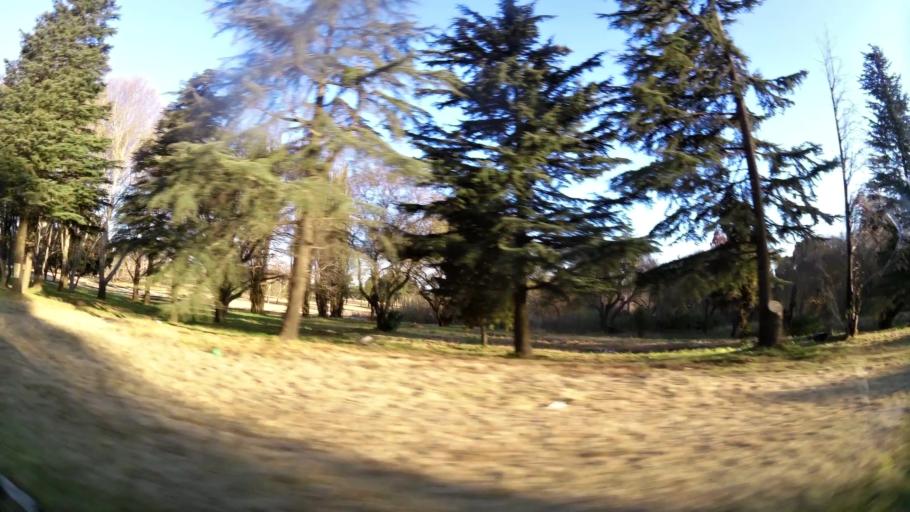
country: ZA
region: Gauteng
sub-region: City of Johannesburg Metropolitan Municipality
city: Roodepoort
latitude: -26.1598
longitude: 27.9074
